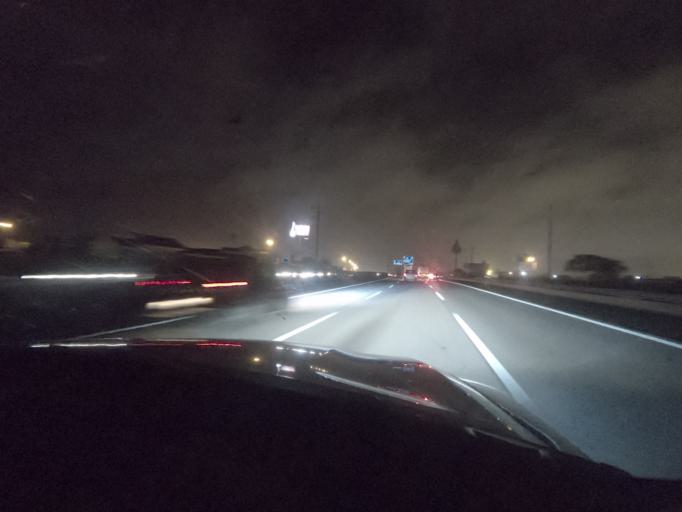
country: PT
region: Lisbon
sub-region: Alenquer
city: Carregado
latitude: 39.0353
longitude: -8.9588
